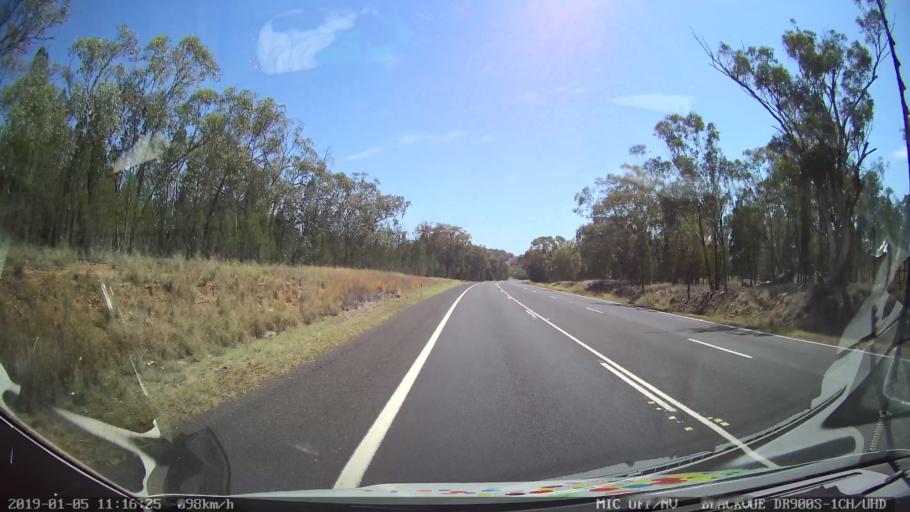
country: AU
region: New South Wales
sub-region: Warrumbungle Shire
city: Coonabarabran
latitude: -31.3391
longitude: 149.2980
